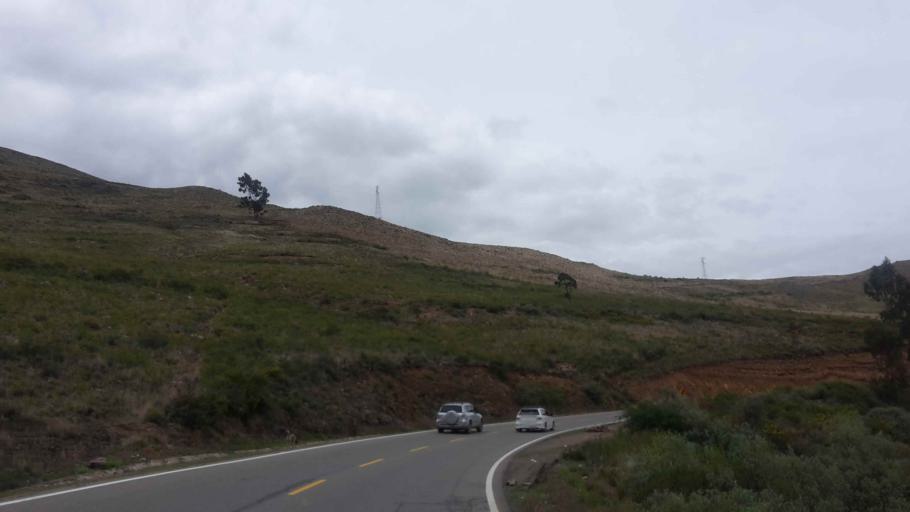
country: BO
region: Cochabamba
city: Arani
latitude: -17.4823
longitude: -65.7696
